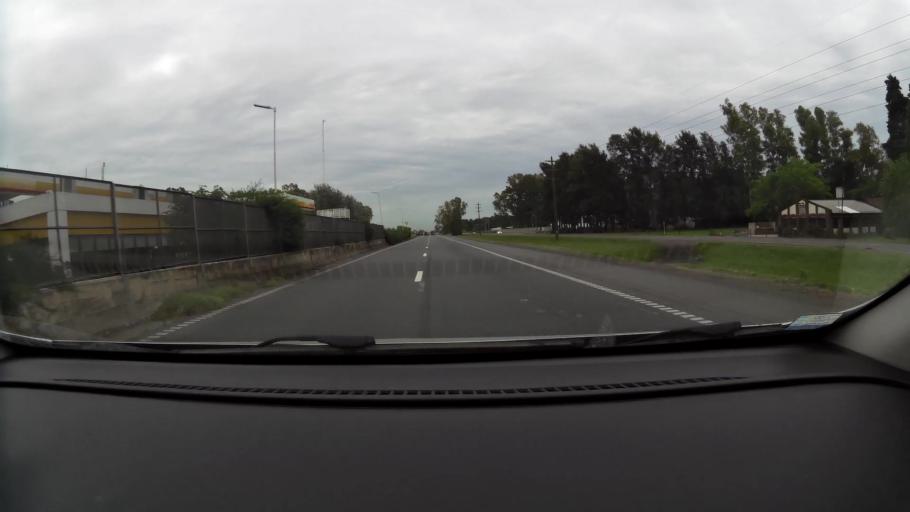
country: AR
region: Buenos Aires
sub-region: Partido de Zarate
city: Zarate
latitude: -34.1104
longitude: -59.1237
